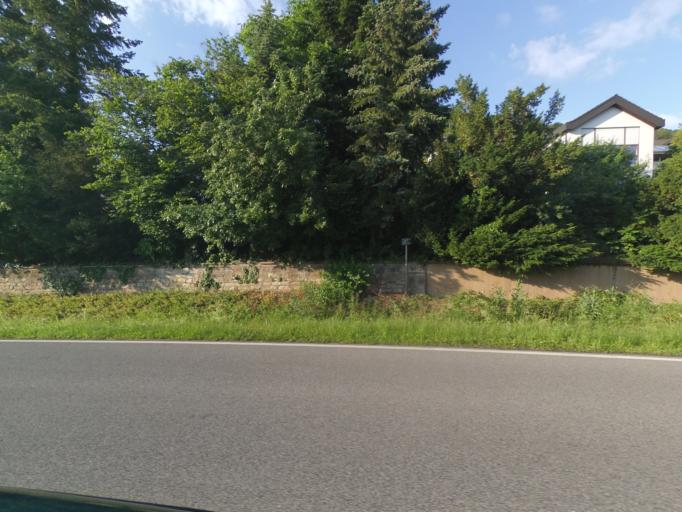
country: DE
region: Bavaria
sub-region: Regierungsbezirk Unterfranken
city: Zeil
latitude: 50.0040
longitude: 10.6061
